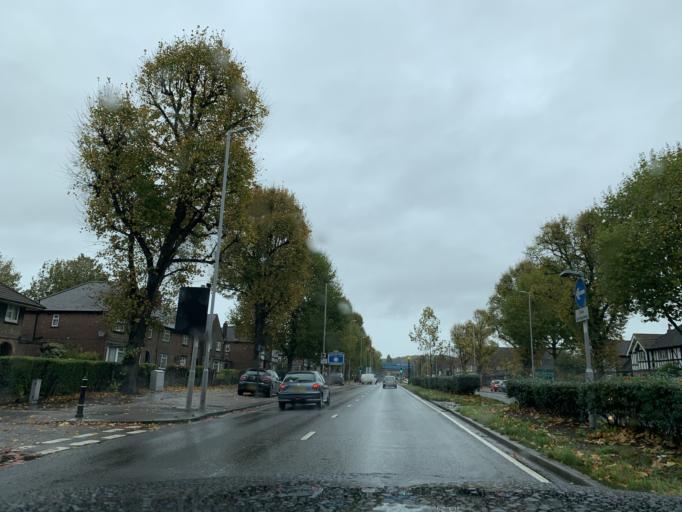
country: GB
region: England
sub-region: Greater London
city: Blackheath
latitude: 51.4544
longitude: 0.0382
